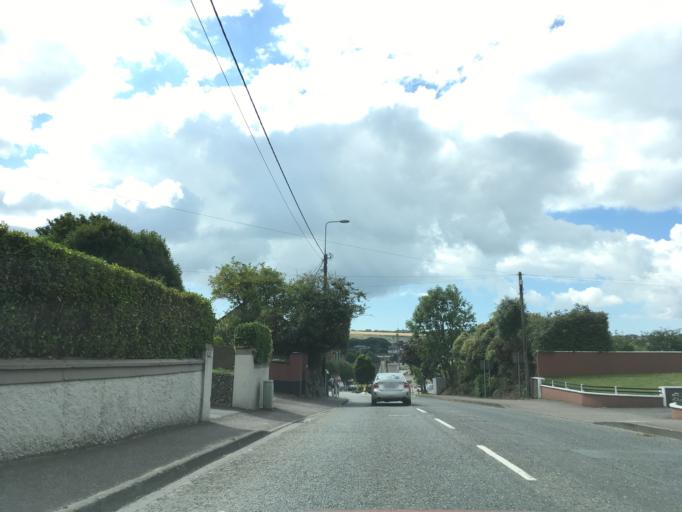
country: IE
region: Munster
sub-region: County Cork
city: Carrigaline
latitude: 51.8177
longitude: -8.3914
